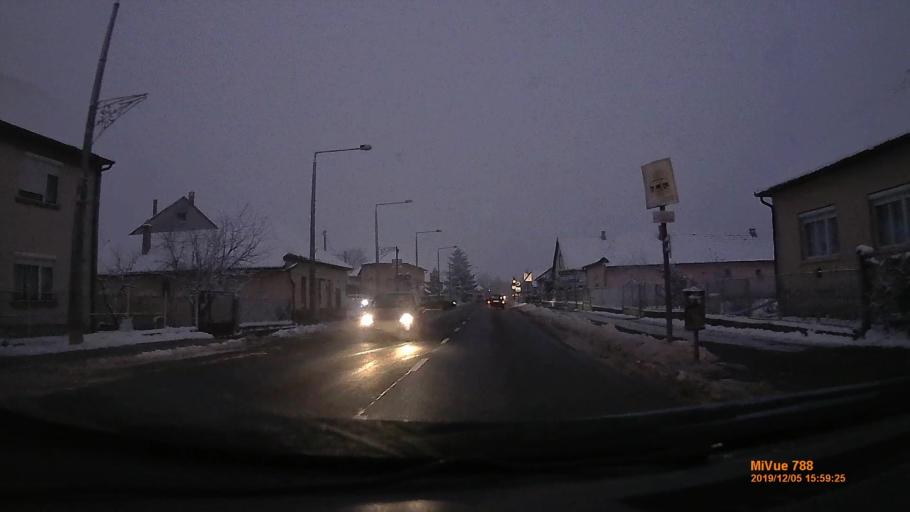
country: HU
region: Borsod-Abauj-Zemplen
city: Tokaj
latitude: 48.1111
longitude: 21.4108
